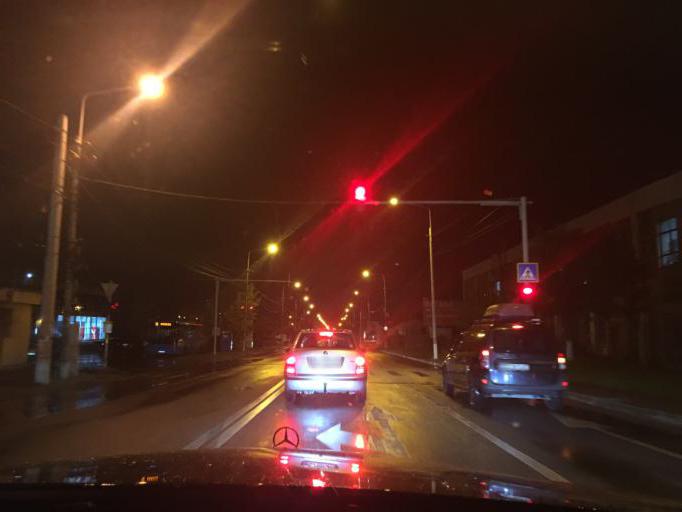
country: RO
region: Bihor
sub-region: Comuna Sanmartin
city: Sanmartin
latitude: 47.0383
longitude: 21.9816
